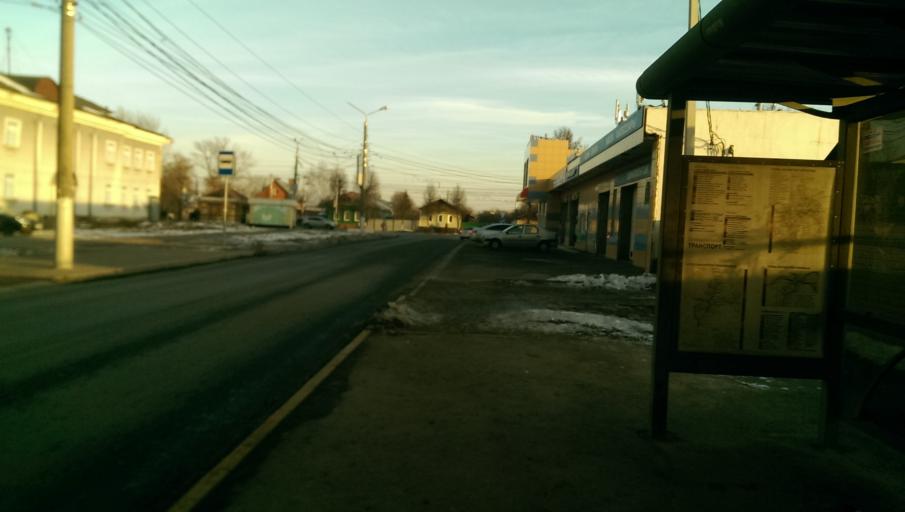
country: RU
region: Tula
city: Tula
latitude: 54.2252
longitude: 37.6268
